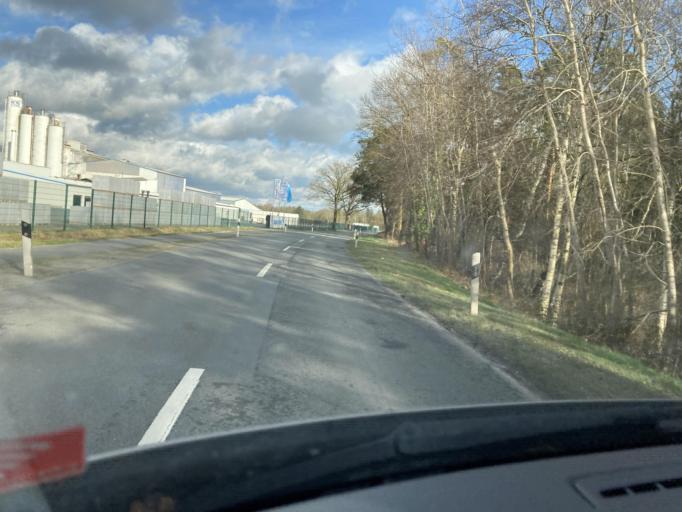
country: DE
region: Lower Saxony
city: Zetel
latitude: 53.4266
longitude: 7.9102
